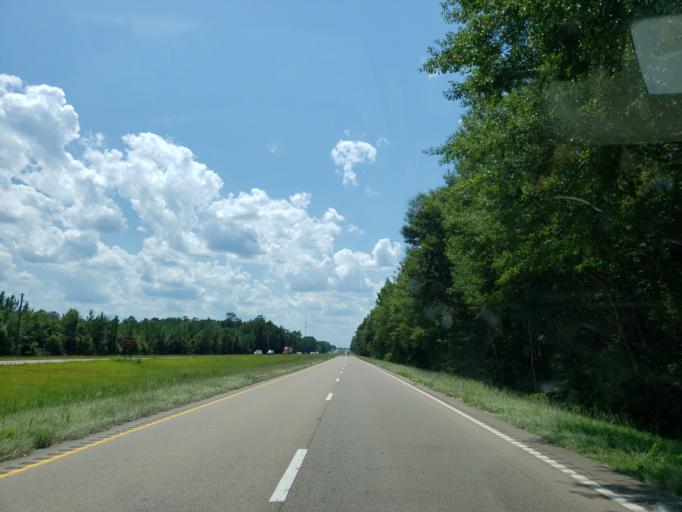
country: US
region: Mississippi
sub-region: Perry County
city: New Augusta
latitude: 31.2012
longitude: -89.0068
